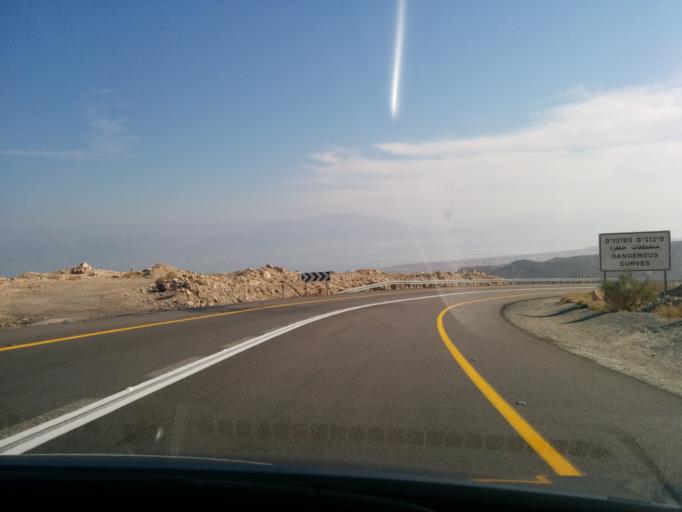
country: IL
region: Southern District
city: `En Boqeq
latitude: 31.1582
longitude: 35.3334
